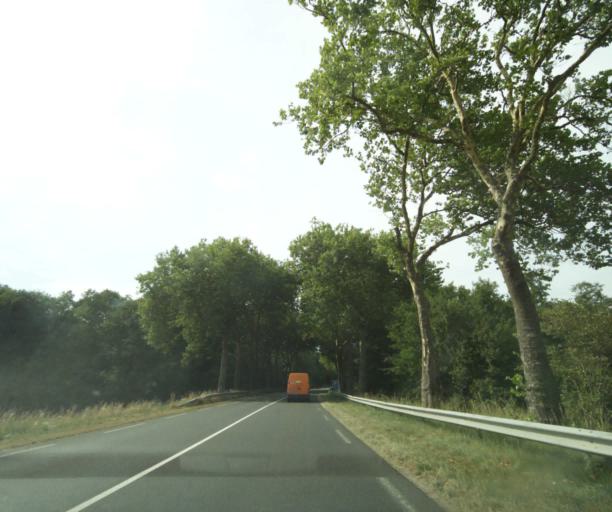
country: FR
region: Centre
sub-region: Departement d'Indre-et-Loire
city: Neuille-Pont-Pierre
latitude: 47.5294
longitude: 0.5677
